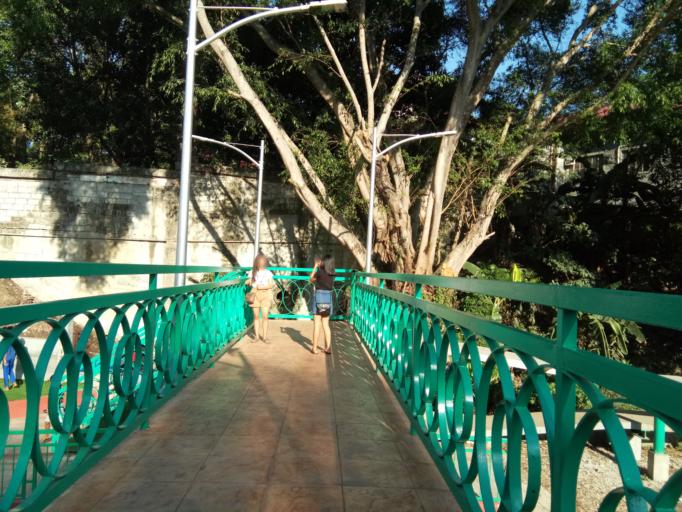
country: PH
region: Calabarzon
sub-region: Province of Cavite
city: Dasmarinas
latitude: 14.3267
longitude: 120.9560
